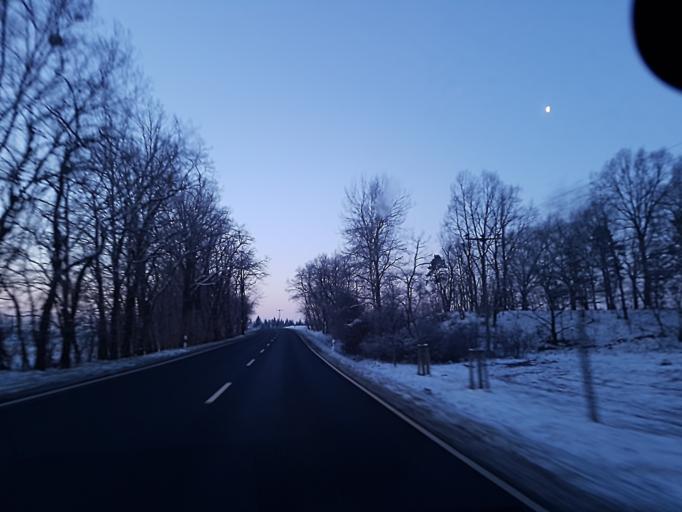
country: DE
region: Brandenburg
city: Muhlberg
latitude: 51.3982
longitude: 13.1879
